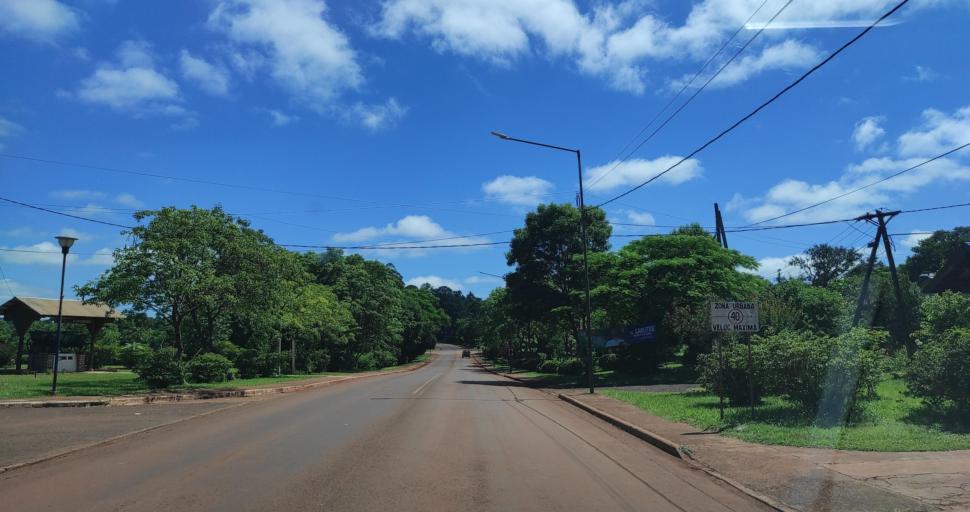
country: AR
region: Misiones
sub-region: Departamento de Veinticinco de Mayo
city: Veinticinco de Mayo
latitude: -27.3862
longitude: -54.7462
